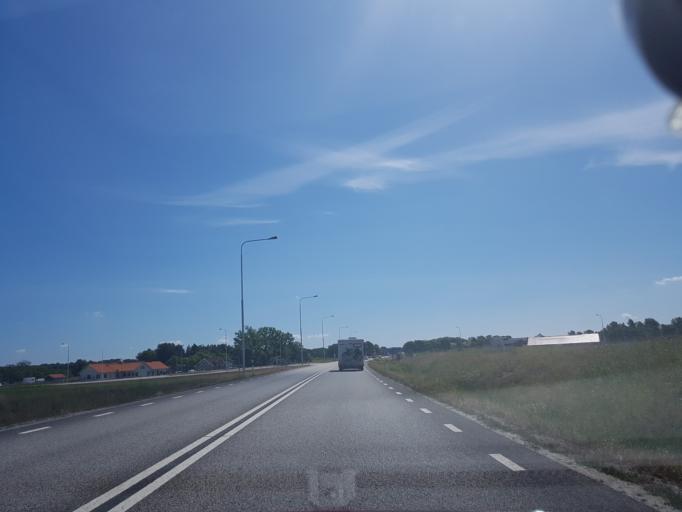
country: SE
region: Vaestra Goetaland
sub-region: Orust
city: Henan
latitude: 58.1502
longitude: 11.5864
